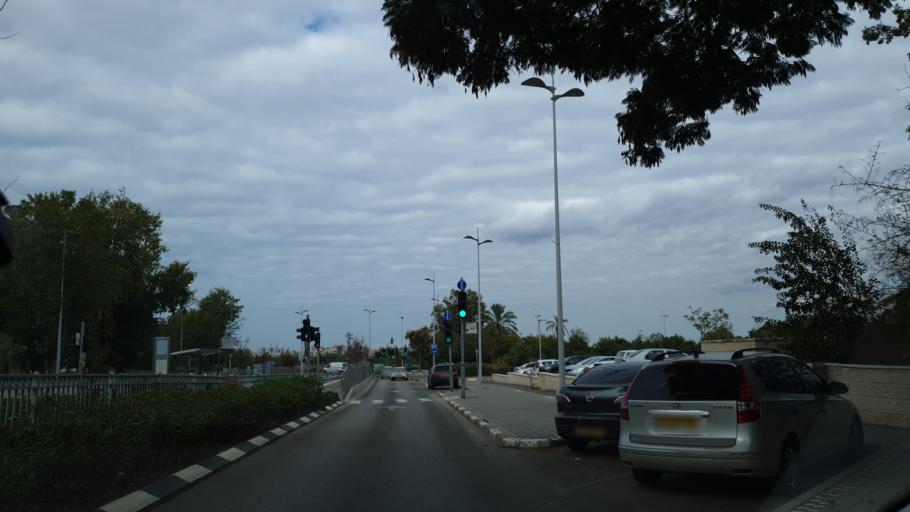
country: IL
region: Haifa
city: Qiryat Ata
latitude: 32.8172
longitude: 35.1134
